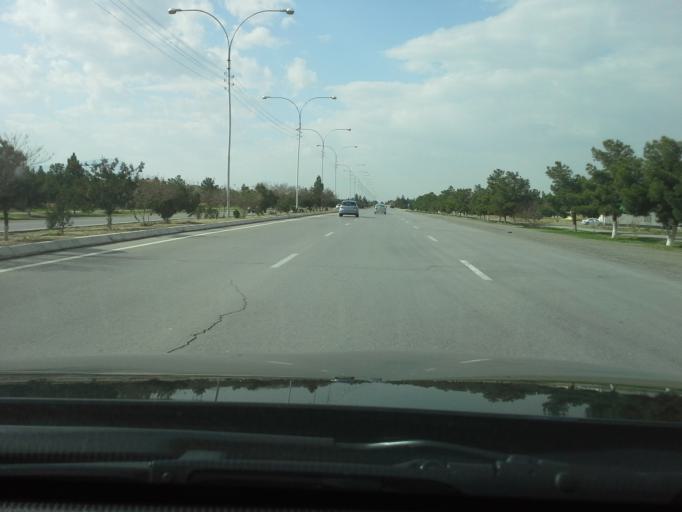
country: TM
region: Ahal
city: Ashgabat
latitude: 37.9643
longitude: 58.3087
